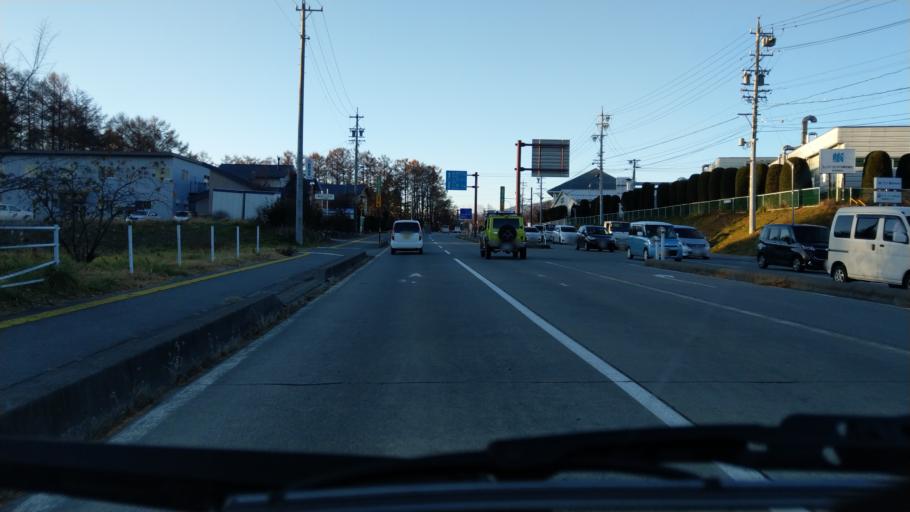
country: JP
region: Nagano
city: Komoro
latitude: 36.2892
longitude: 138.4727
